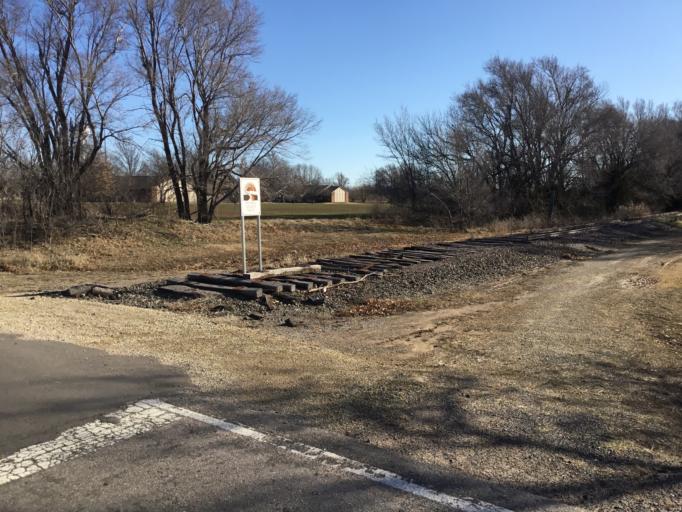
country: US
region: Kansas
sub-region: Sedgwick County
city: Saint Marys
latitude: 37.6562
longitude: -97.6796
